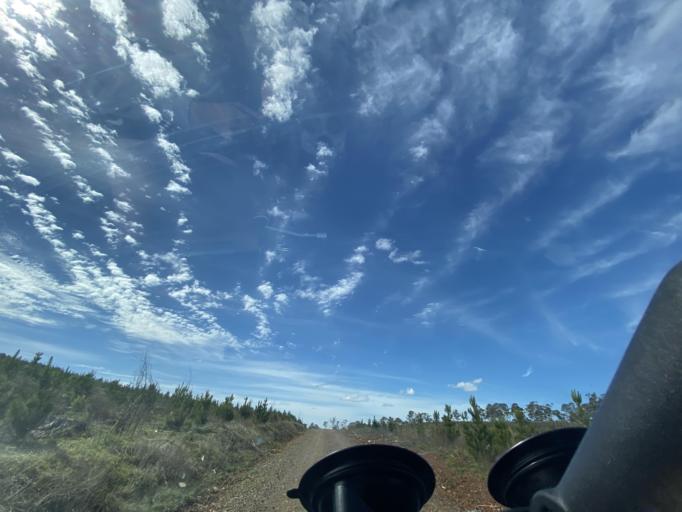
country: AU
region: Victoria
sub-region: Mansfield
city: Mansfield
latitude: -36.8292
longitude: 146.1023
